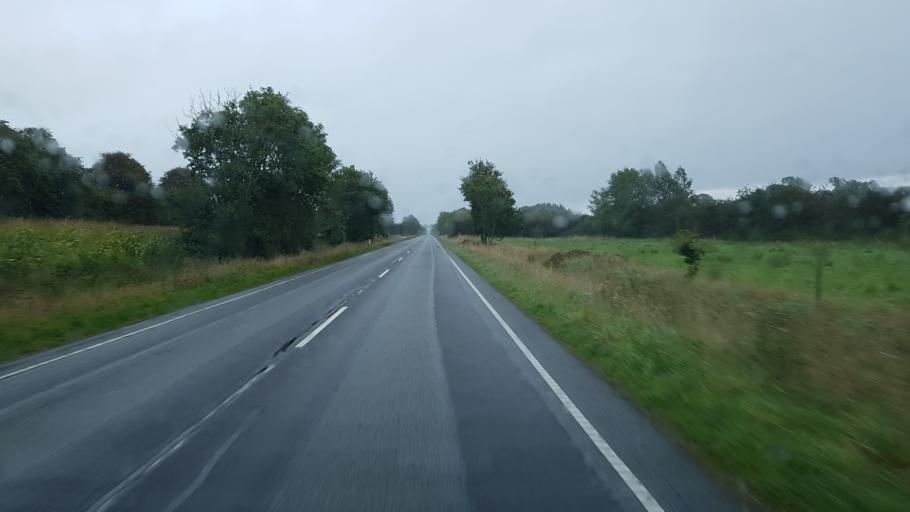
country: DK
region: South Denmark
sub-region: Kolding Kommune
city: Vamdrup
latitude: 55.3488
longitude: 9.2455
